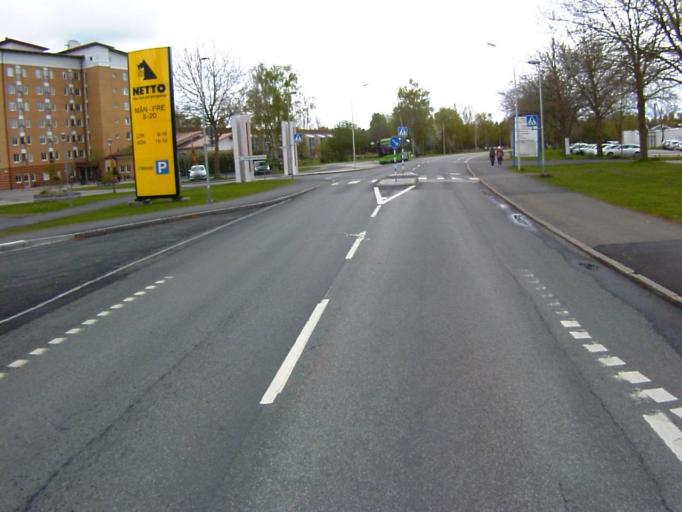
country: SE
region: Skane
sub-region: Kristianstads Kommun
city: Kristianstad
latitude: 56.0432
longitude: 14.1770
